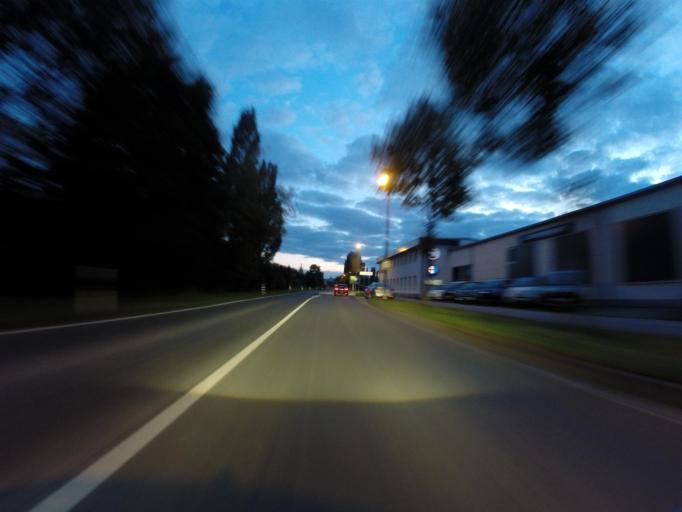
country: DE
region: Thuringia
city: Jena
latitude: 50.9411
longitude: 11.6036
